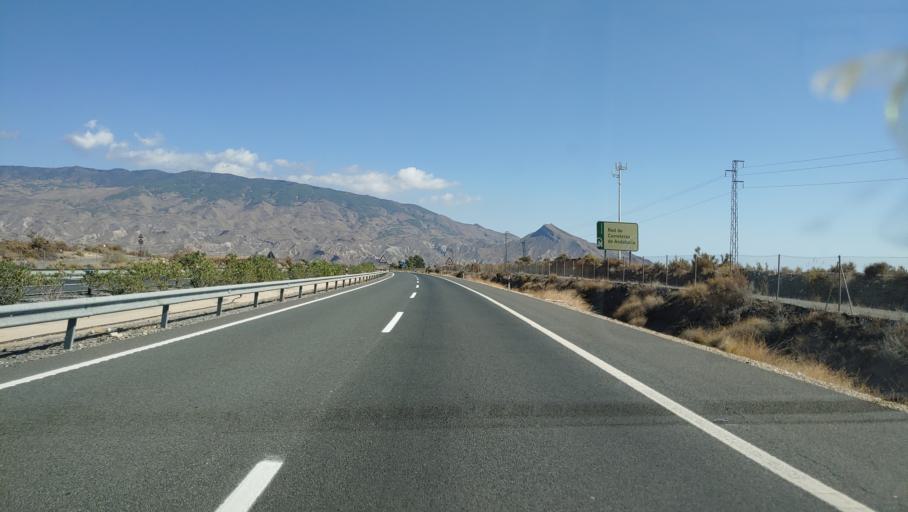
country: ES
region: Andalusia
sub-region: Provincia de Almeria
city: Tabernas
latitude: 37.0409
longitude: -2.4677
